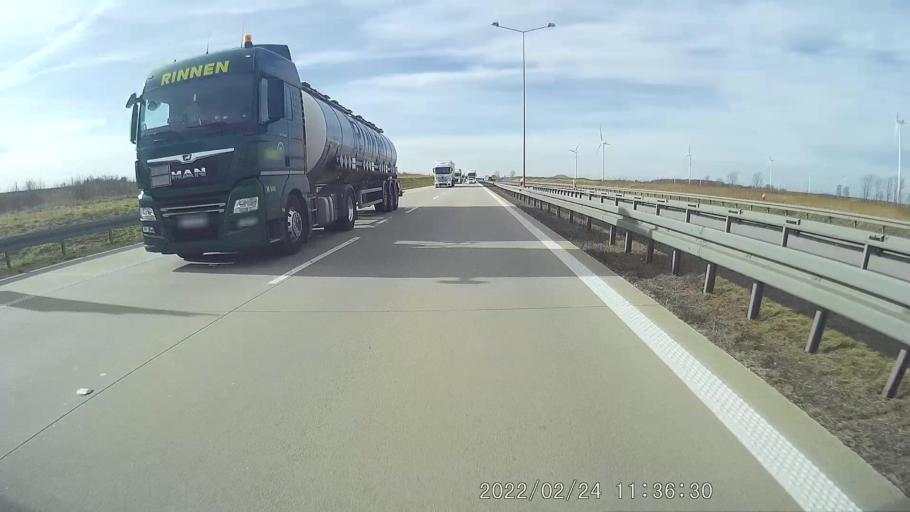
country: PL
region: Lower Silesian Voivodeship
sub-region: Powiat polkowicki
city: Przemkow
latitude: 51.5223
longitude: 15.8071
